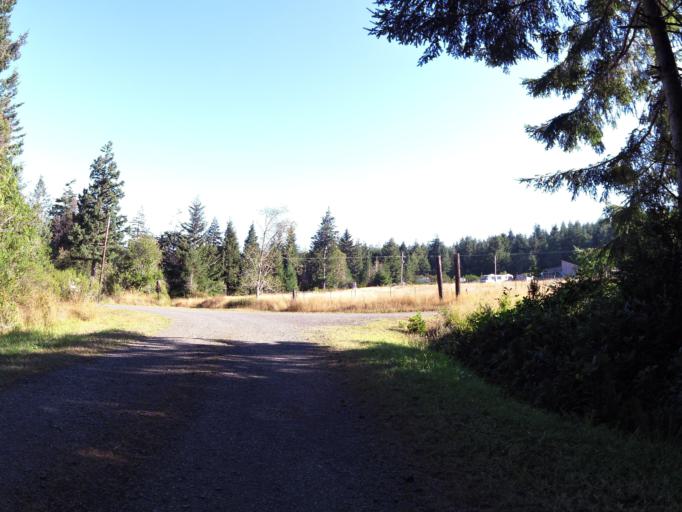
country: US
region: Oregon
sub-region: Coos County
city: Bandon
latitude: 43.0349
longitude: -124.3909
